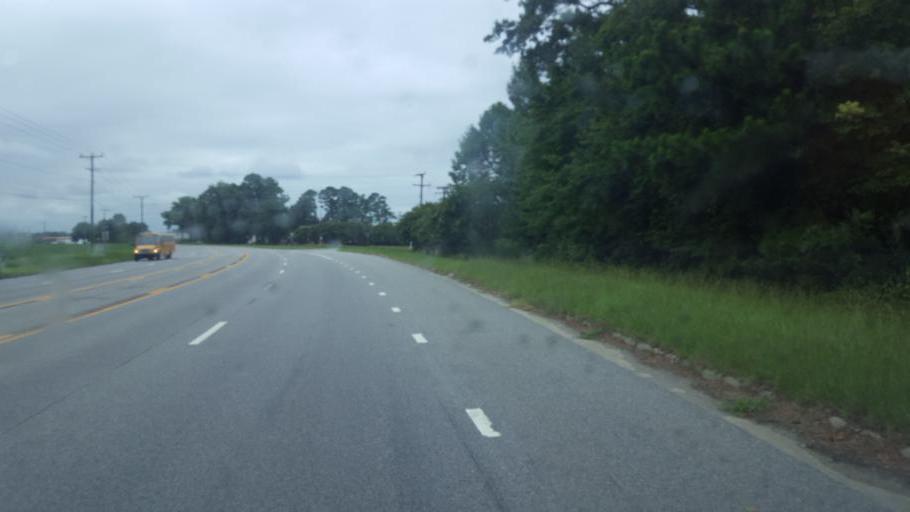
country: US
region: North Carolina
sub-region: Currituck County
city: Currituck
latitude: 36.4456
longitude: -76.0137
